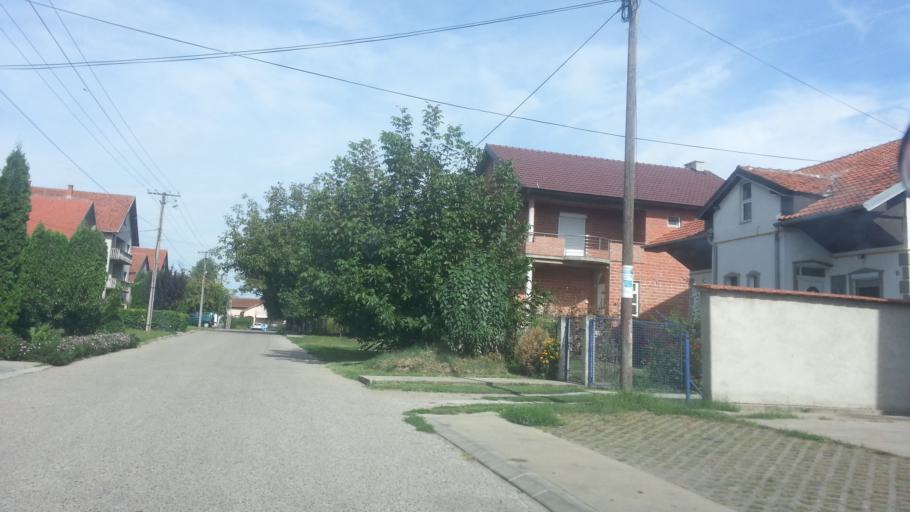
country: RS
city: Novi Banovci
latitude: 44.9484
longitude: 20.2781
